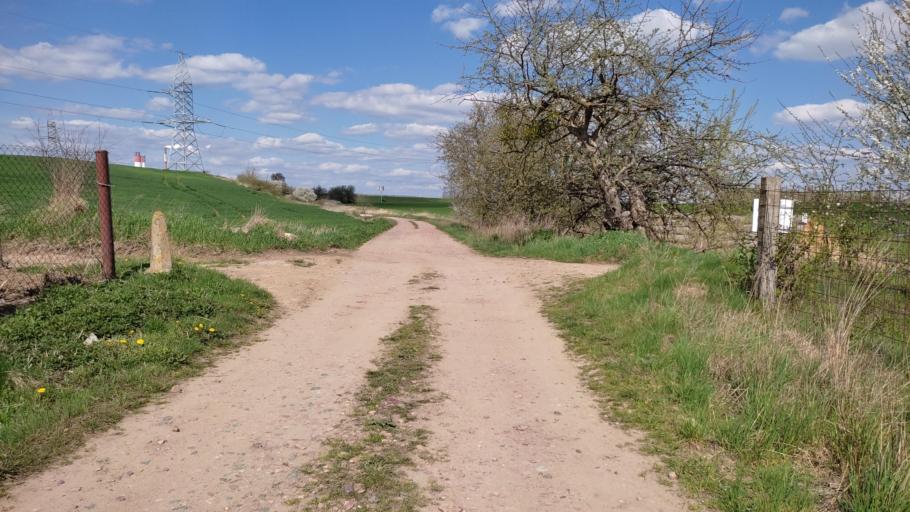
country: BY
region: Grodnenskaya
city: Hrodna
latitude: 53.6575
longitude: 23.9057
